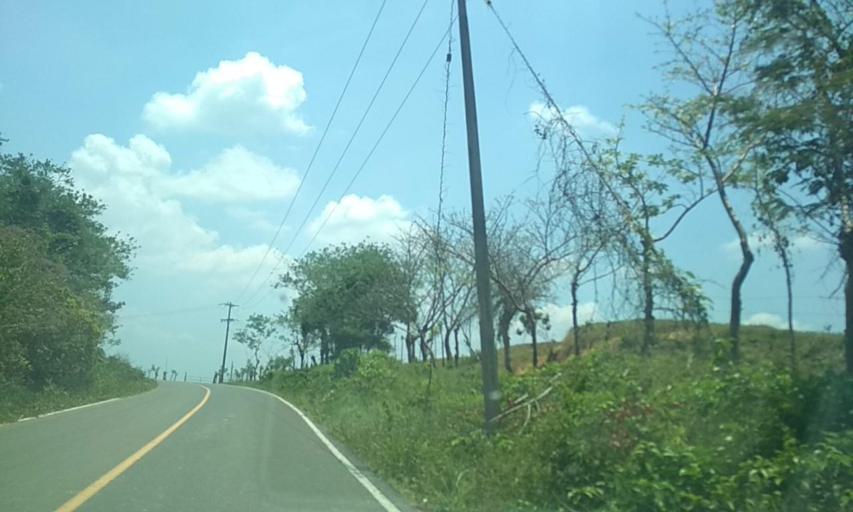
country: MX
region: Tabasco
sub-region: Huimanguillo
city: Francisco Rueda
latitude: 17.7592
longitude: -94.0566
